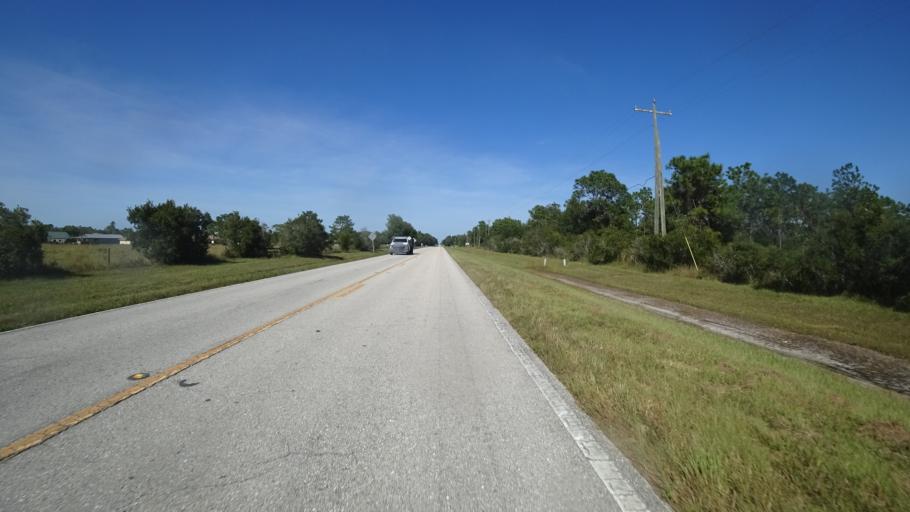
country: US
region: Florida
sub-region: Sarasota County
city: Fruitville
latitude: 27.4023
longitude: -82.3040
